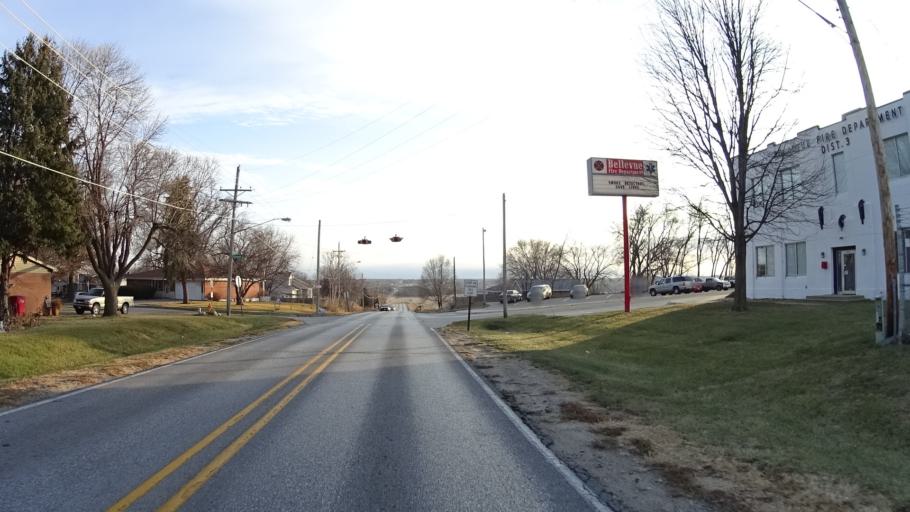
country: US
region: Nebraska
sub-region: Sarpy County
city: La Vista
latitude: 41.1676
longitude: -95.9672
